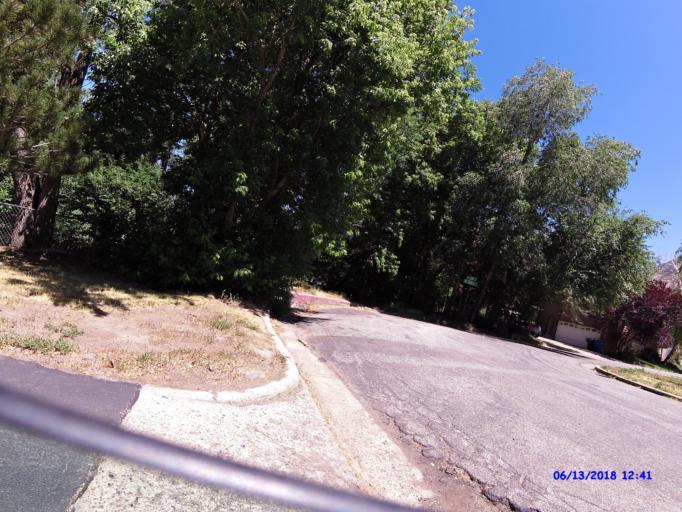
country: US
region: Utah
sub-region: Weber County
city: South Ogden
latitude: 41.2007
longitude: -111.9474
